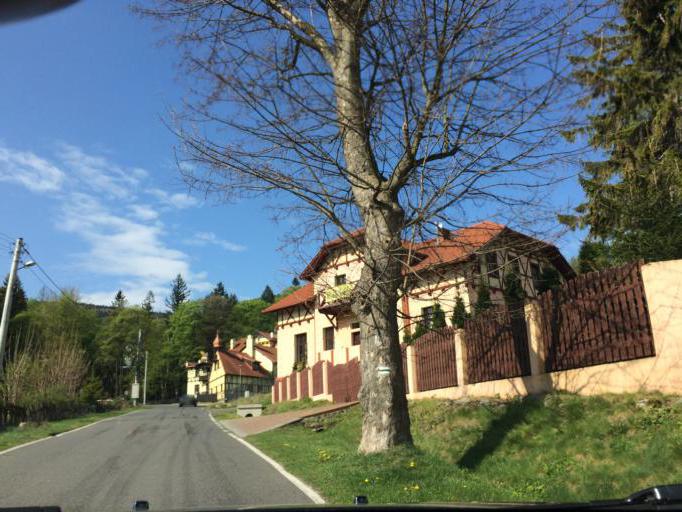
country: PL
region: Lower Silesian Voivodeship
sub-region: Powiat klodzki
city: Jugow
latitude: 50.6694
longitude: 16.5388
